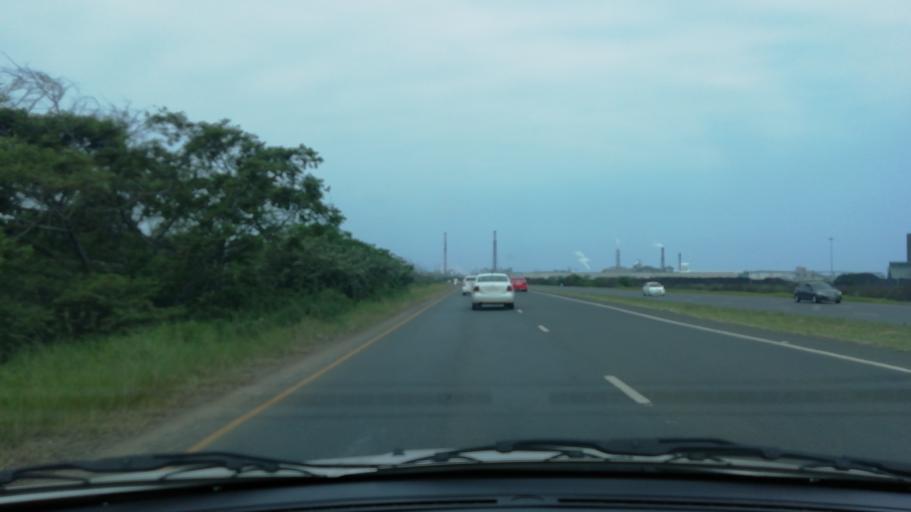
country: ZA
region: KwaZulu-Natal
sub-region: uThungulu District Municipality
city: Richards Bay
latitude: -28.7718
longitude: 32.0220
